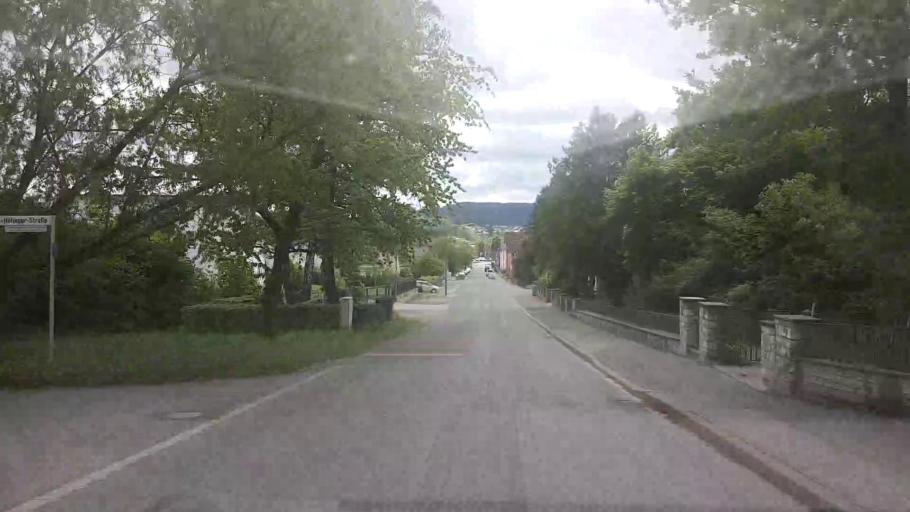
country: DE
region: Bavaria
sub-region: Upper Franconia
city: Lichtenfels
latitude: 50.1561
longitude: 11.0566
